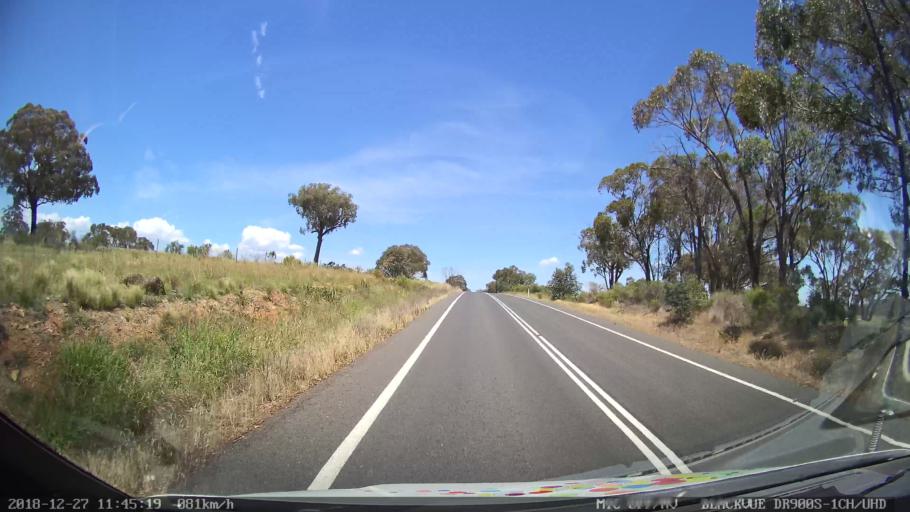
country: AU
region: New South Wales
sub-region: Bathurst Regional
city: Perthville
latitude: -33.5812
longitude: 149.4712
